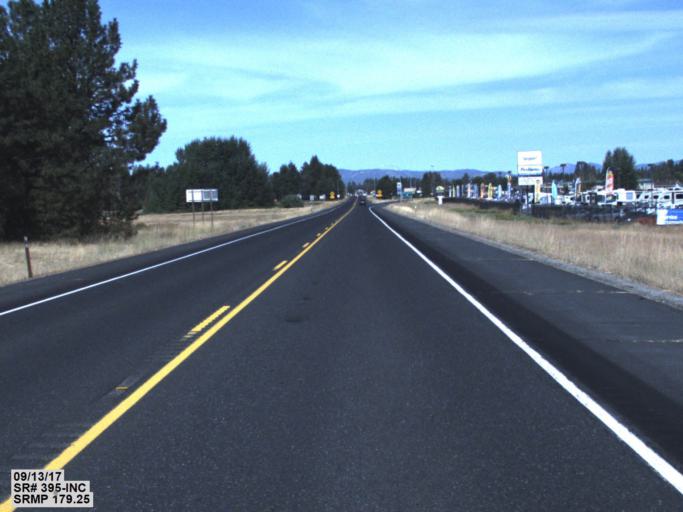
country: US
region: Washington
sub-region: Spokane County
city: Deer Park
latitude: 47.9393
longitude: -117.4741
